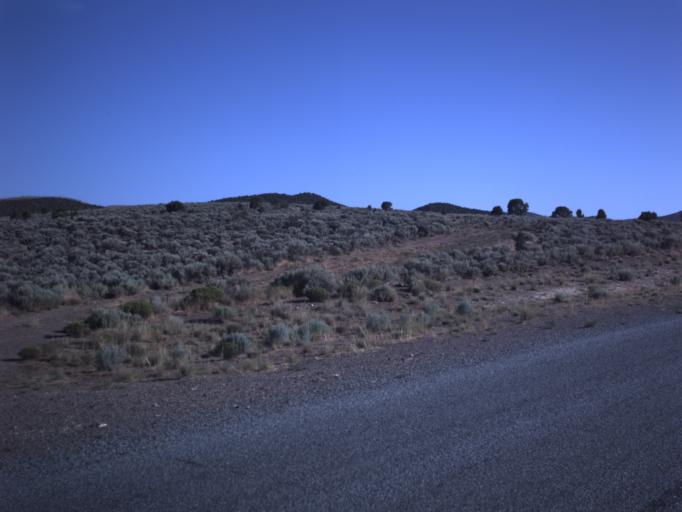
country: US
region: Utah
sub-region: Iron County
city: Parowan
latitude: 38.0352
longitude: -112.9981
